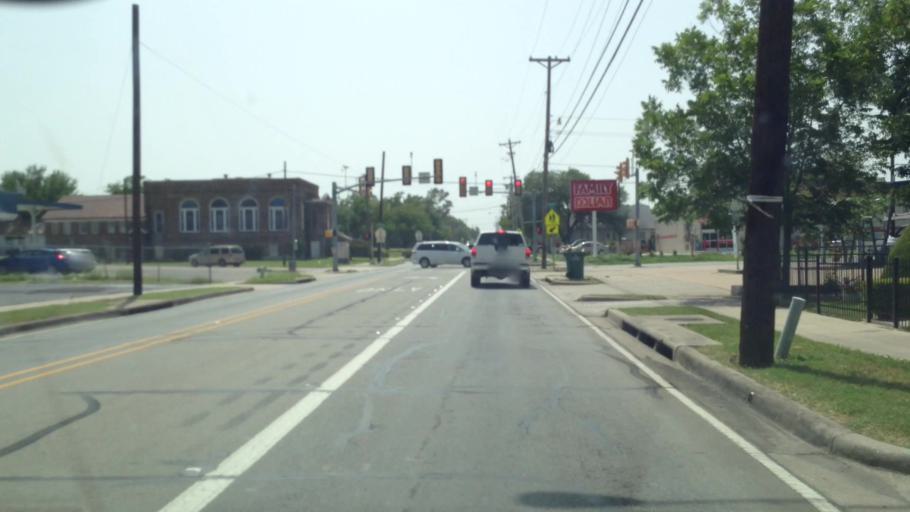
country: US
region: Texas
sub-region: Hunt County
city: Greenville
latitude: 33.1400
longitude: -96.1193
